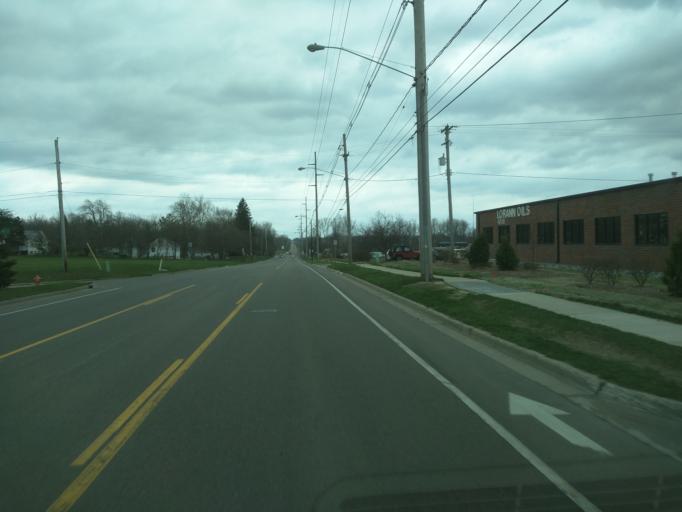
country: US
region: Michigan
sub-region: Ingham County
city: Holt
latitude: 42.6880
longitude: -84.5234
